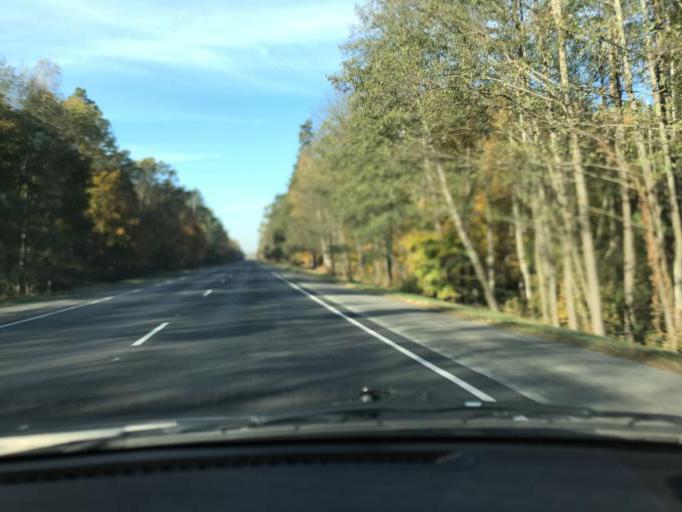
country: BY
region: Brest
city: Mikashevichy
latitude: 52.2455
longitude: 27.4172
